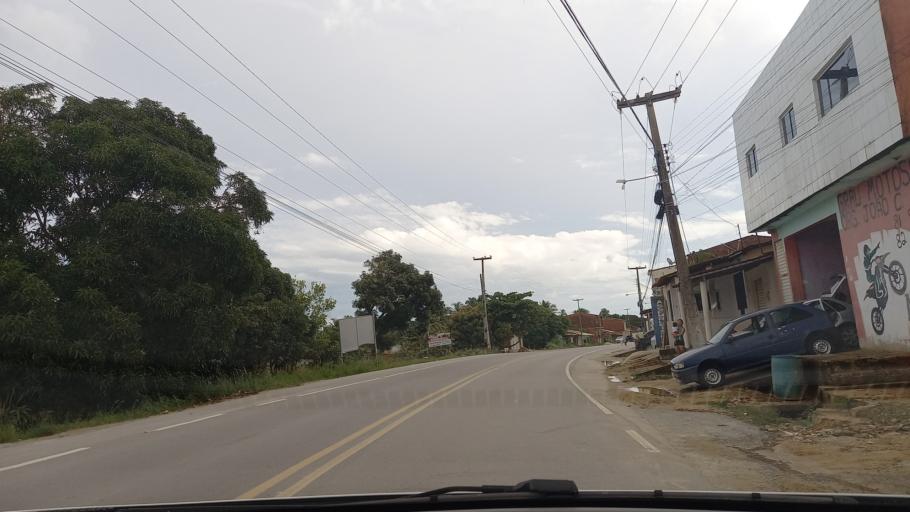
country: BR
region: Alagoas
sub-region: Maragogi
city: Maragogi
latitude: -8.9851
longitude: -35.1971
